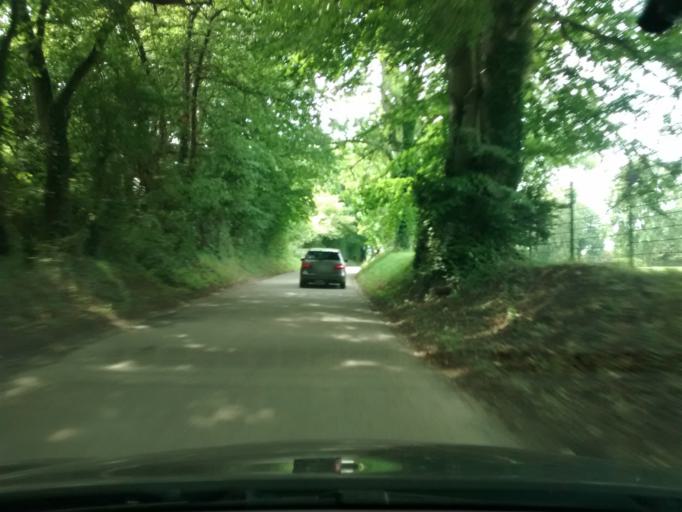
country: FR
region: Lower Normandy
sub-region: Departement du Calvados
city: Deauville
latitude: 49.3357
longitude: 0.0763
